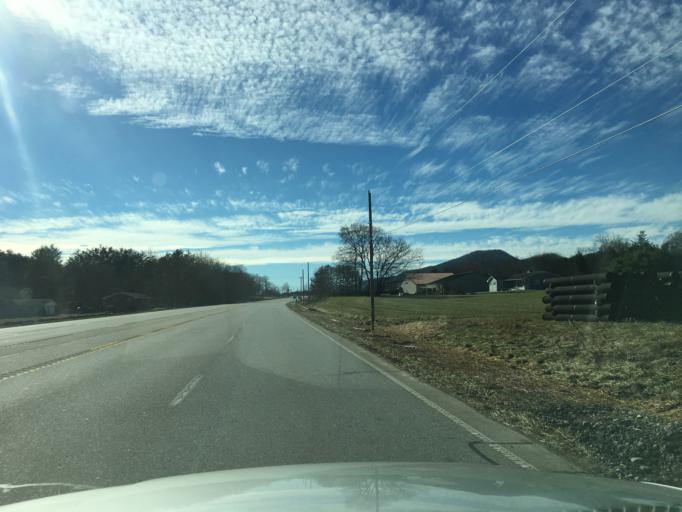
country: US
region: North Carolina
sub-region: Henderson County
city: Mills River
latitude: 35.3799
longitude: -82.5749
